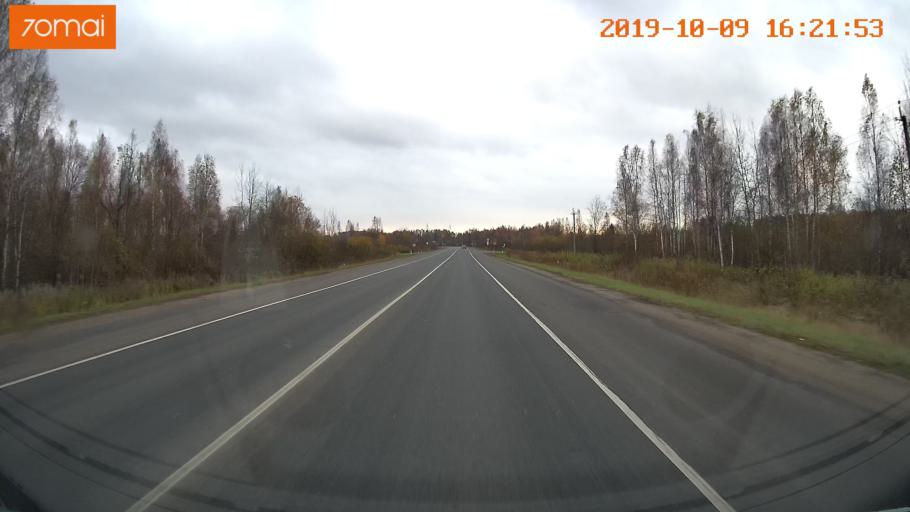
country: RU
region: Kostroma
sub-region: Kostromskoy Rayon
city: Kostroma
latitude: 57.6851
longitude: 40.8877
